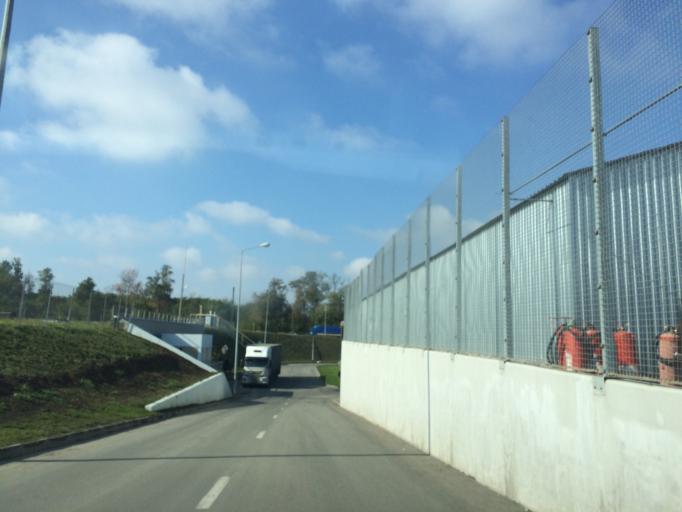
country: RU
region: Rostov
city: Aksay
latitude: 47.2872
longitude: 39.8460
